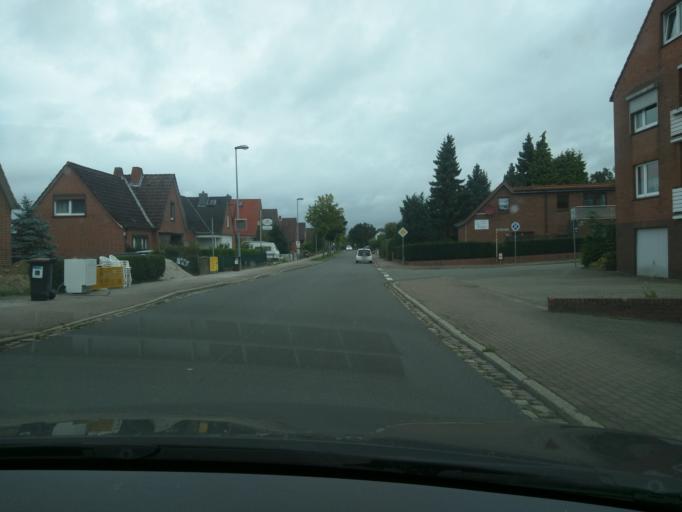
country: DE
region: Schleswig-Holstein
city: Lauenburg
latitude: 53.3795
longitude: 10.5549
